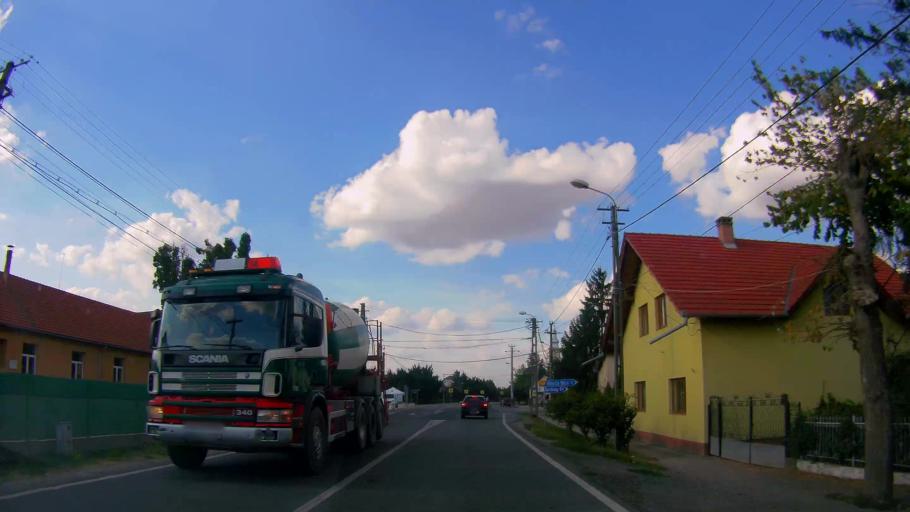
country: RO
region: Satu Mare
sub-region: Comuna Turulung
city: Turulung
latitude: 47.9321
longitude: 23.0835
